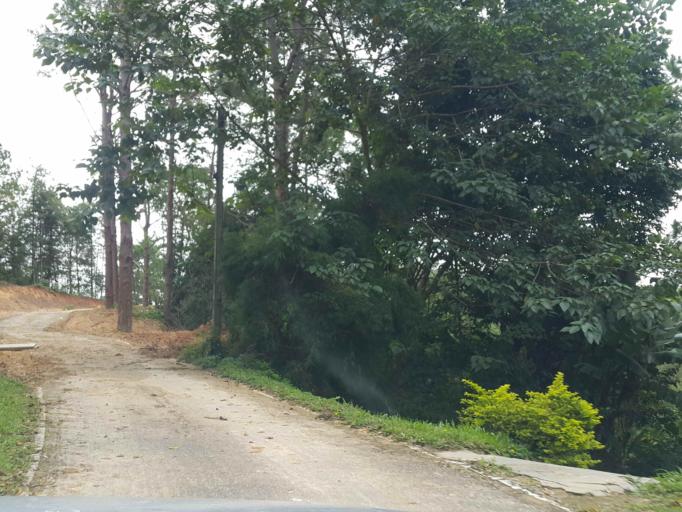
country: TH
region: Tak
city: Tak
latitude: 16.7823
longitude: 98.9279
